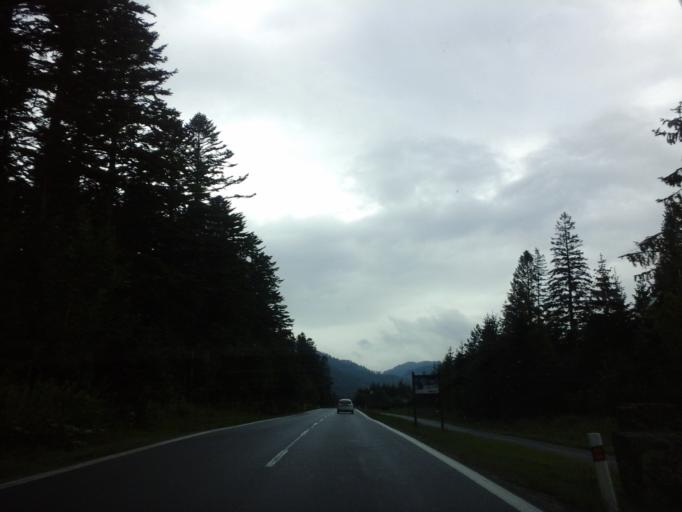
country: SK
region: Presovsky
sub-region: Okres Poprad
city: Zdiar
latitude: 49.2166
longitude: 20.3397
